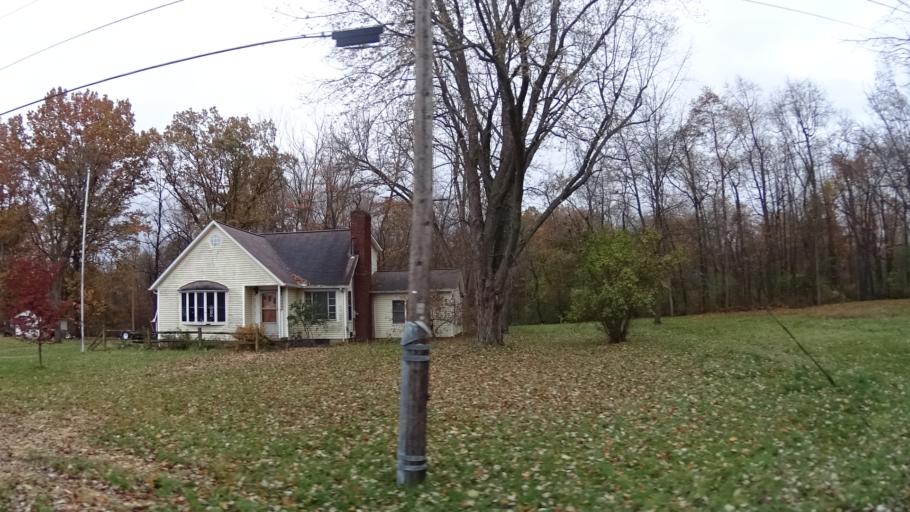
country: US
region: Ohio
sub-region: Lorain County
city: Elyria
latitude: 41.3993
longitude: -82.1340
